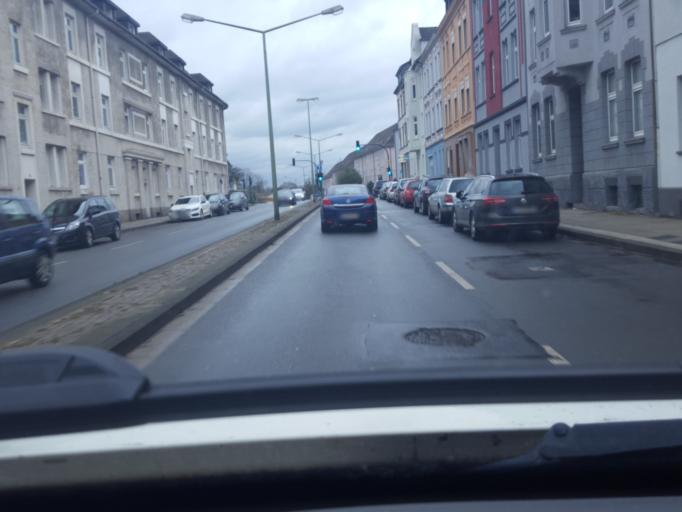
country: DE
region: North Rhine-Westphalia
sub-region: Regierungsbezirk Dusseldorf
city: Essen
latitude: 51.4520
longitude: 6.9640
